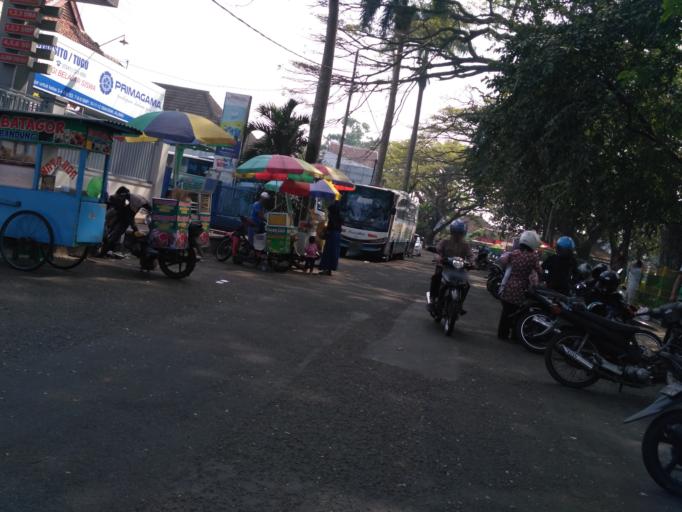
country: ID
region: East Java
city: Malang
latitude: -7.9769
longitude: 112.6363
